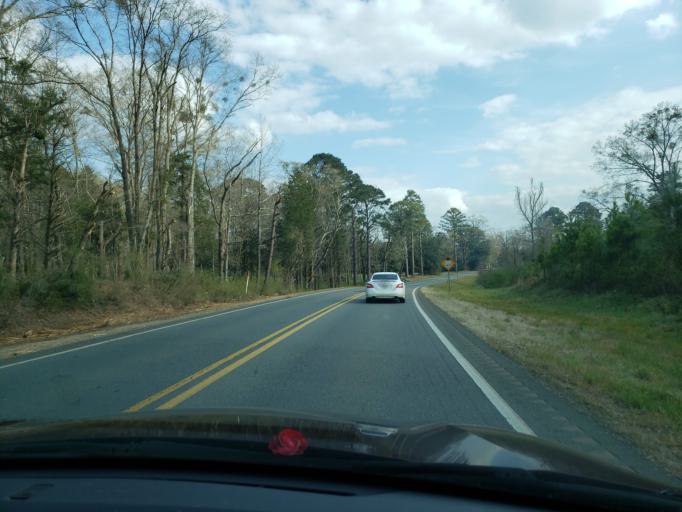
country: US
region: Alabama
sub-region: Hale County
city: Greensboro
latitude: 32.7084
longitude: -87.6089
